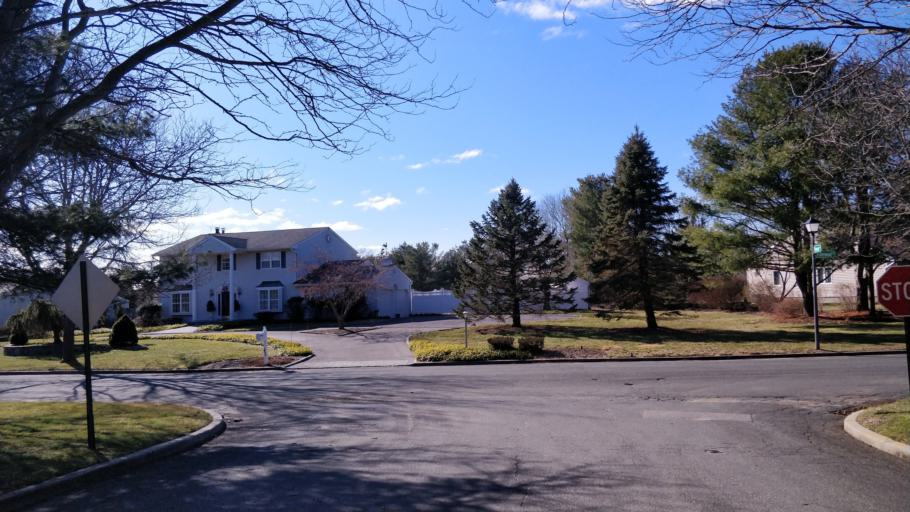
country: US
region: New York
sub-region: Suffolk County
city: Head of the Harbor
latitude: 40.8925
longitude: -73.1392
